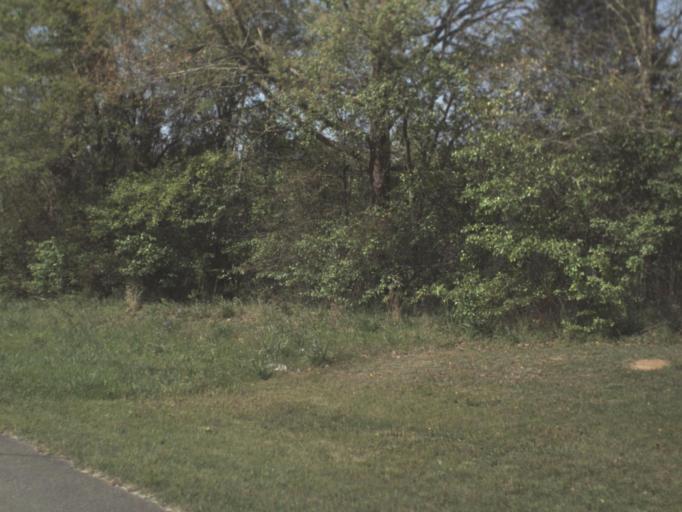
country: US
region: Florida
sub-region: Jackson County
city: Graceville
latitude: 30.9125
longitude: -85.4315
